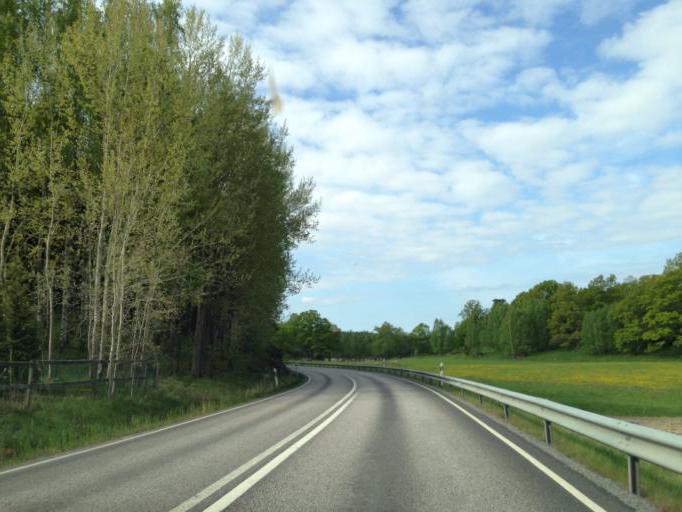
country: SE
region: Soedermanland
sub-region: Flens Kommun
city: Malmkoping
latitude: 59.0125
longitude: 16.8461
